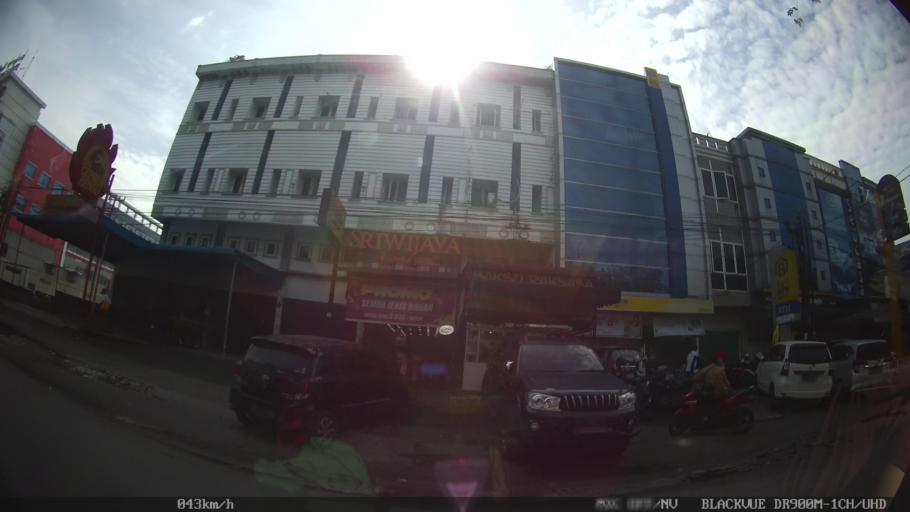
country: ID
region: North Sumatra
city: Medan
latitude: 3.5721
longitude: 98.6427
